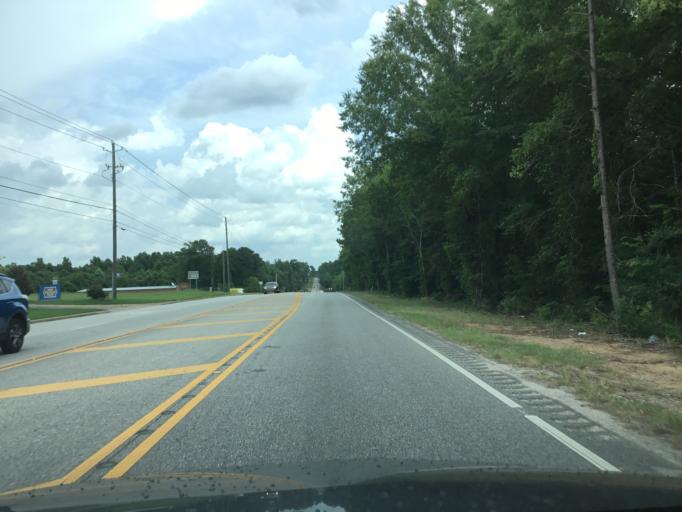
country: US
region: Alabama
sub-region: Montgomery County
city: Pike Road
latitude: 32.3468
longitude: -86.0901
